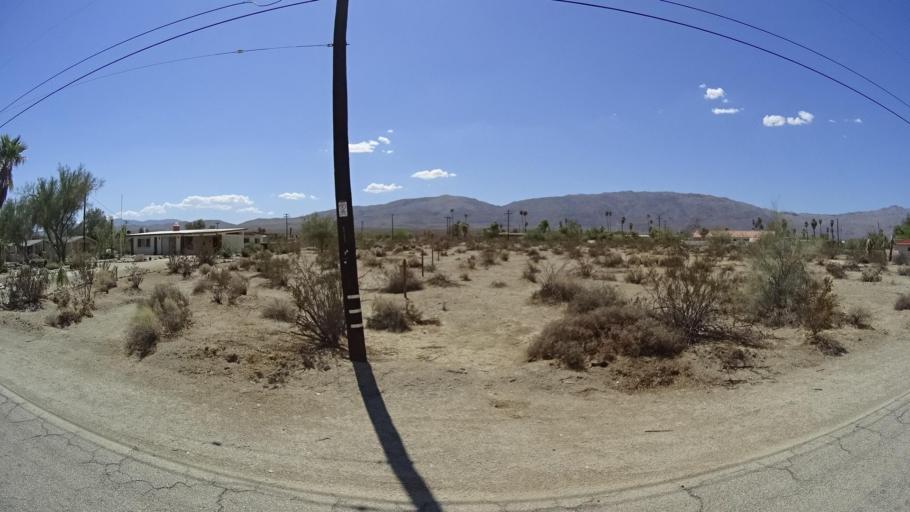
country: US
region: California
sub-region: San Diego County
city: Borrego Springs
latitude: 33.2092
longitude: -116.3337
